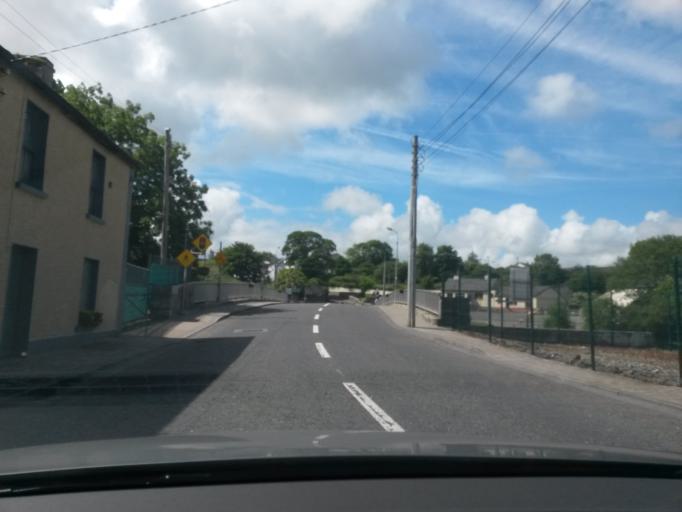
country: IE
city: Ballisodare
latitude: 54.2098
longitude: -8.5090
